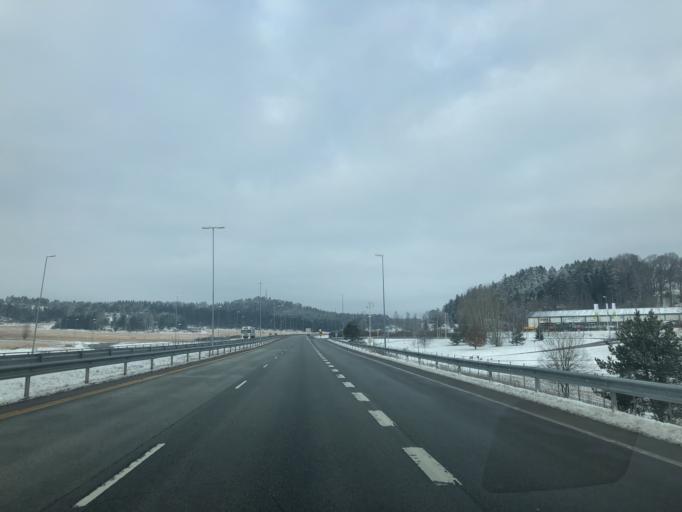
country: NO
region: Ostfold
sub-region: Sarpsborg
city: Skjeberg
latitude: 59.1775
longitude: 11.2083
